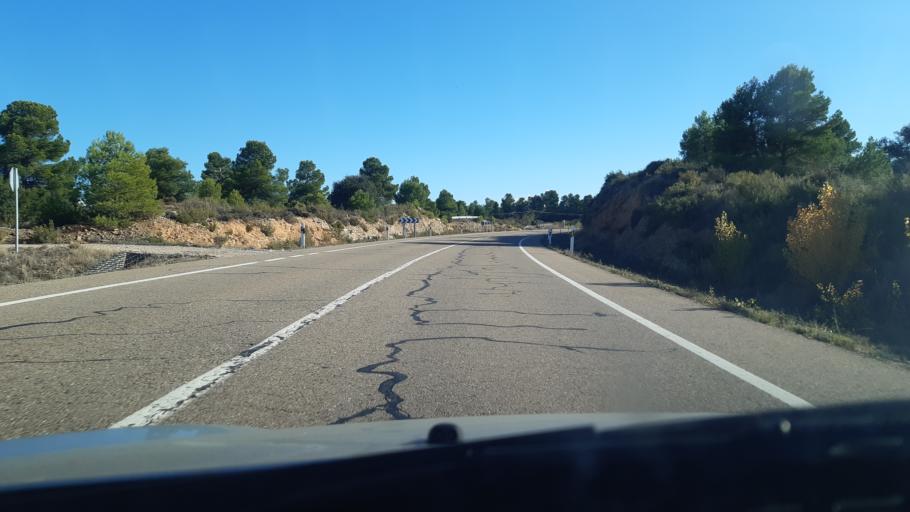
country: ES
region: Aragon
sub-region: Provincia de Teruel
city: Valjunquera
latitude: 40.9506
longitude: -0.0110
